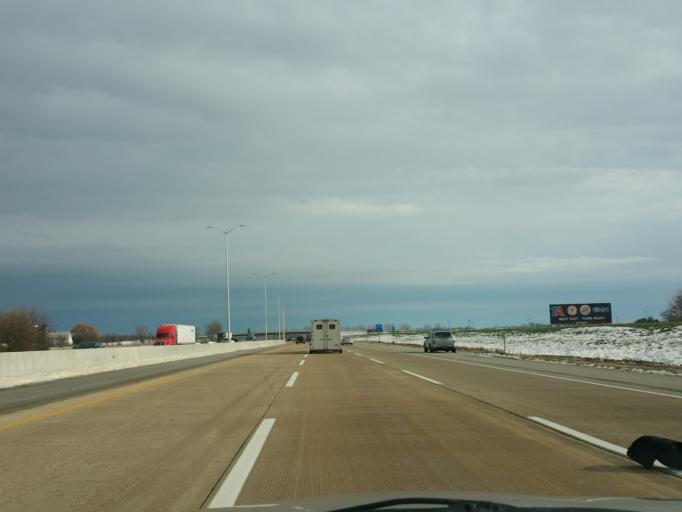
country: US
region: Illinois
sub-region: Boone County
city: Belvidere
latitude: 42.2220
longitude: -88.7556
